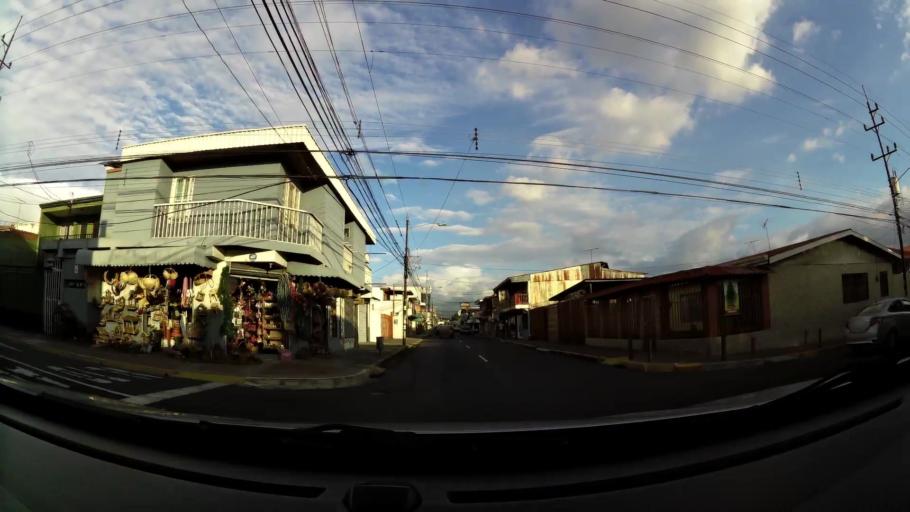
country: CR
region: Heredia
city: Heredia
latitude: 9.9968
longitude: -84.1218
